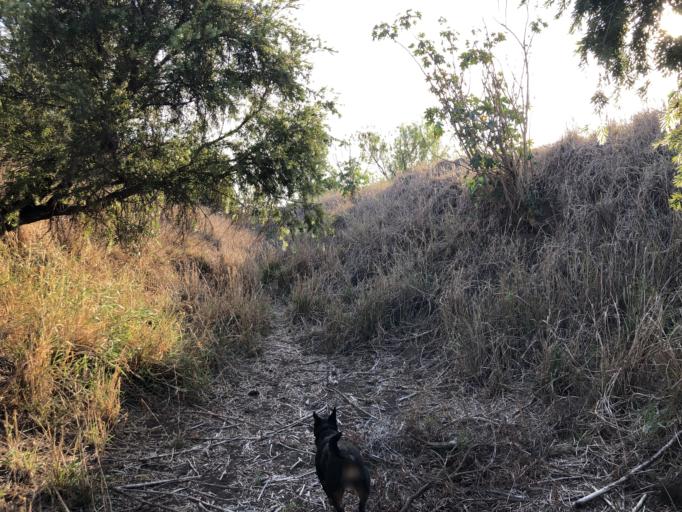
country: AU
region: Queensland
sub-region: Lockyer Valley
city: Gatton
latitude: -27.5839
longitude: 152.3494
